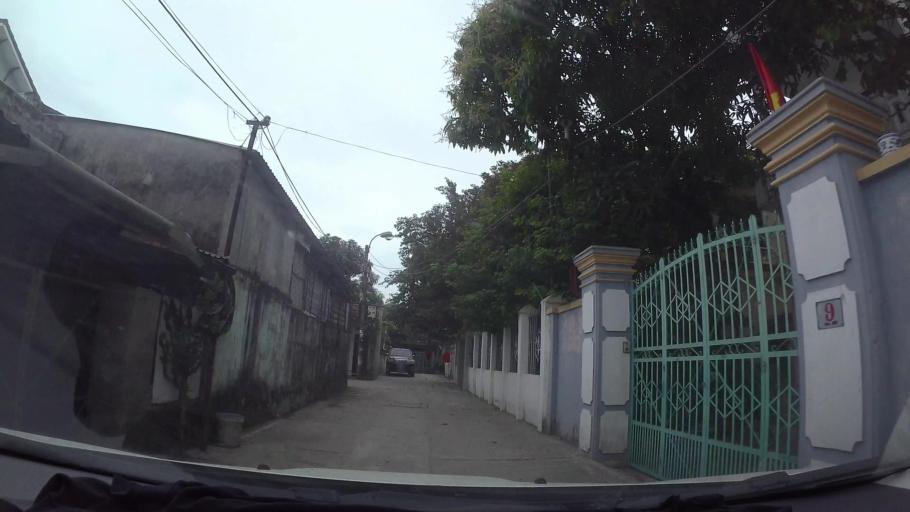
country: VN
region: Da Nang
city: Lien Chieu
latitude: 16.0858
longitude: 108.1424
